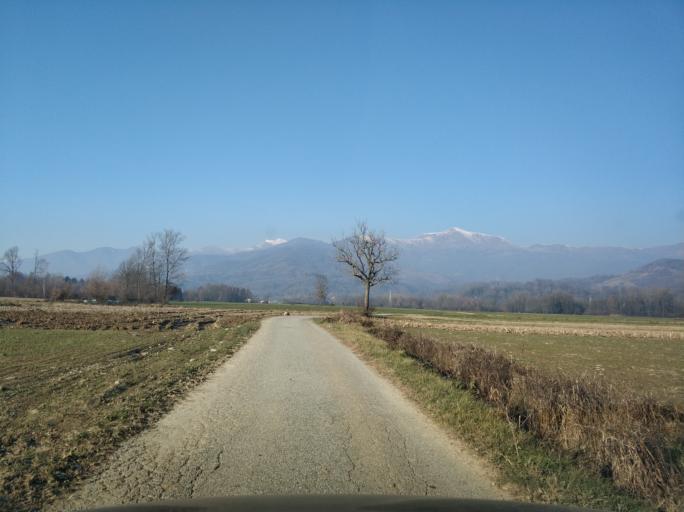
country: IT
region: Piedmont
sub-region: Provincia di Torino
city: Levone
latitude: 45.3095
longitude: 7.6252
